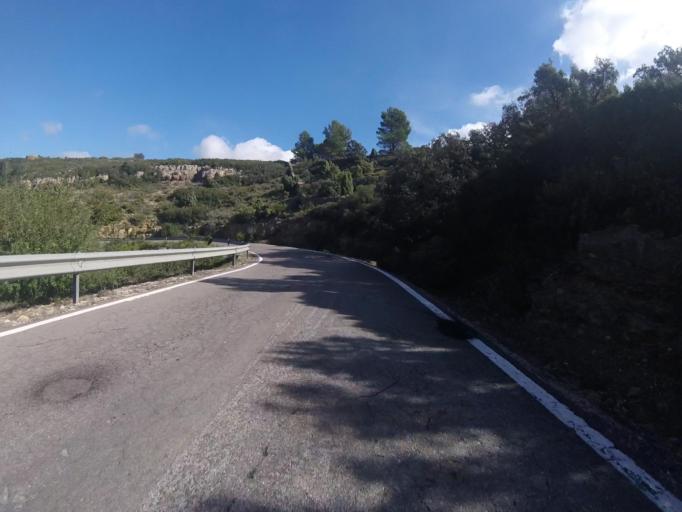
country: ES
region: Valencia
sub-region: Provincia de Castello
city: Albocasser
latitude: 40.3495
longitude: 0.0498
